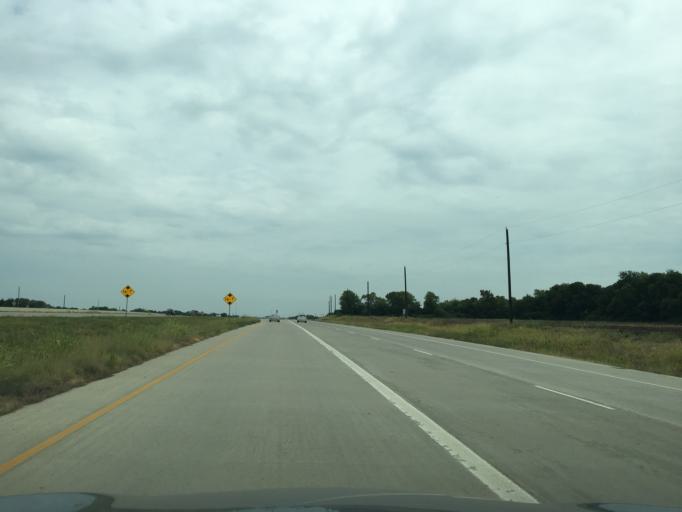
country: US
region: Texas
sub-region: Collin County
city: Melissa
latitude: 33.2785
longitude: -96.5922
